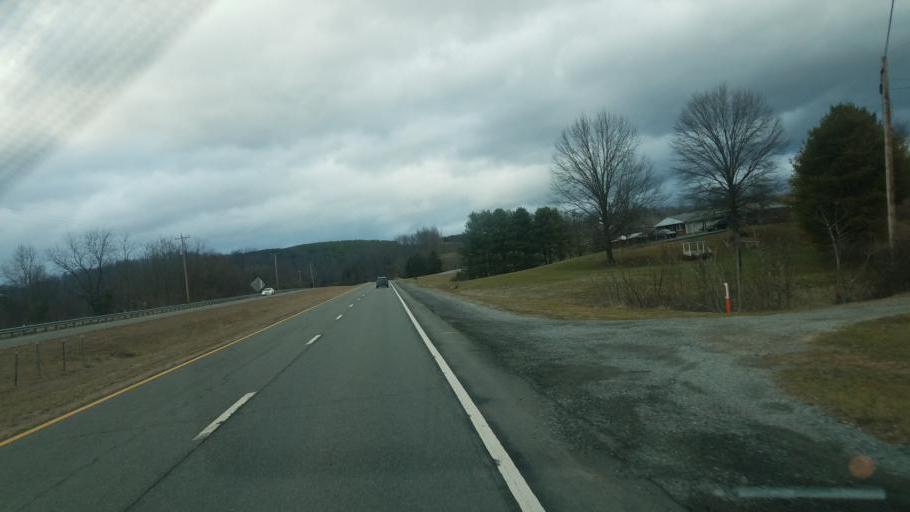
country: US
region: Virginia
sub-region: Giles County
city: Pearisburg
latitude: 37.2607
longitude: -80.7114
